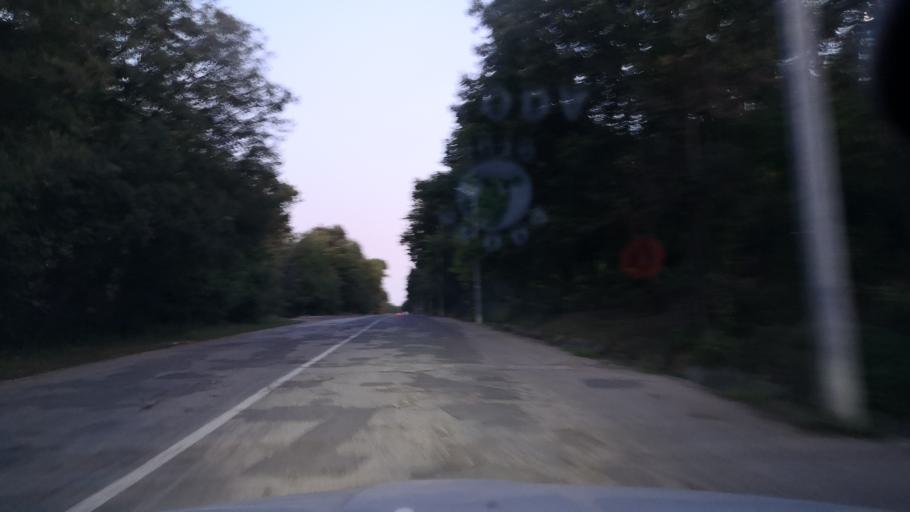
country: MD
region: Orhei
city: Orhei
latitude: 47.3959
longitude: 28.8210
